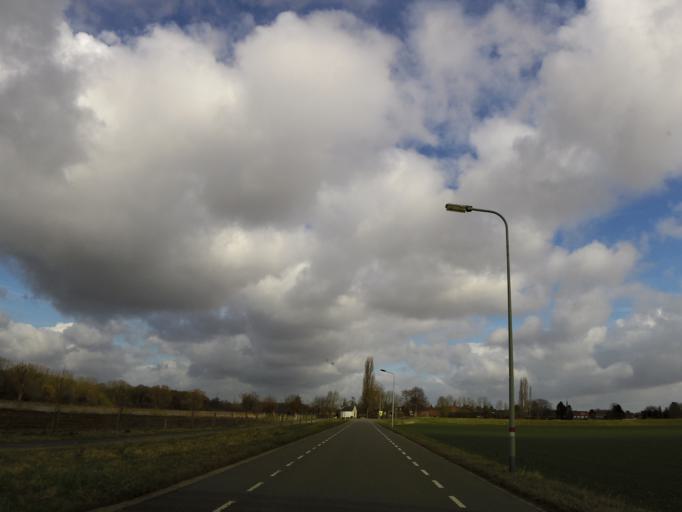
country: NL
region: Limburg
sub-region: Gemeente Maastricht
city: Maastricht
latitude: 50.8934
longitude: 5.6952
